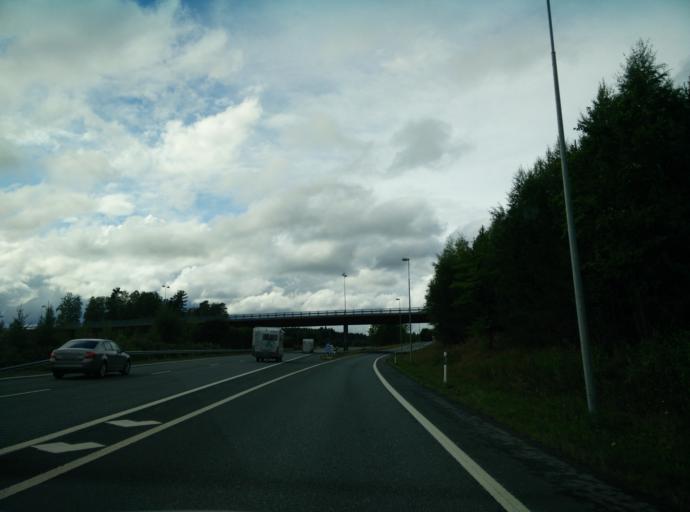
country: FI
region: Haeme
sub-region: Haemeenlinna
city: Kalvola
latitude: 61.0975
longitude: 24.1683
